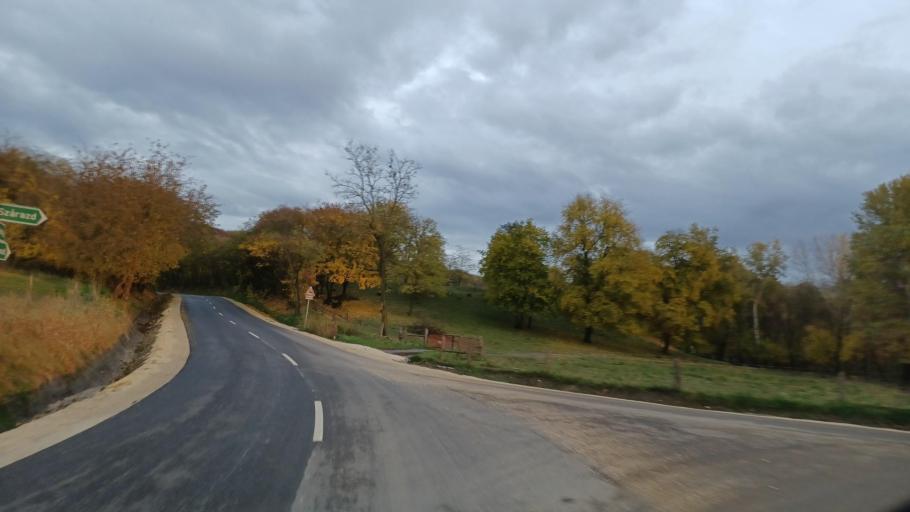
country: HU
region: Tolna
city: Gyonk
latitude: 46.5799
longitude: 18.4422
